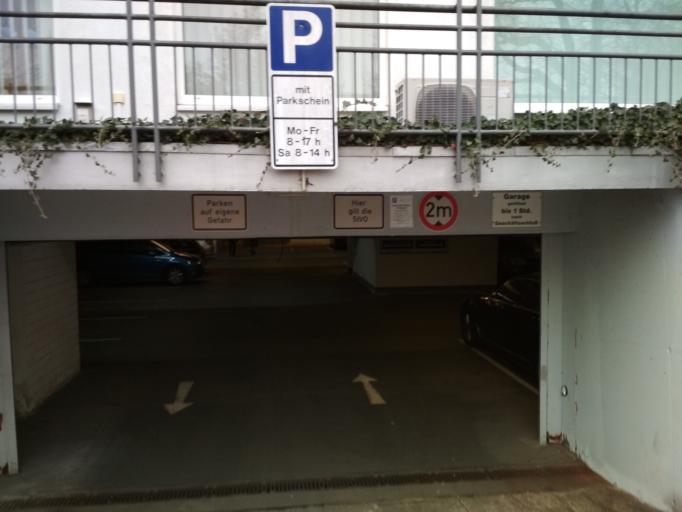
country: DE
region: Lower Saxony
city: Gifhorn
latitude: 52.4875
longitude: 10.5473
